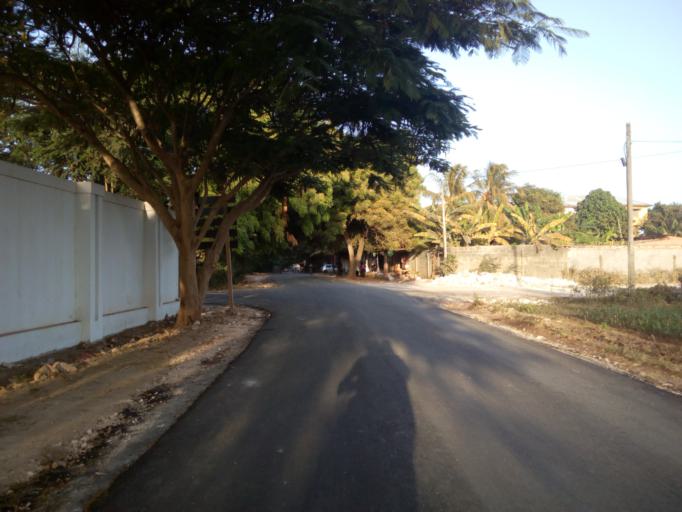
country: TZ
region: Zanzibar Urban/West
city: Zanzibar
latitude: -6.2087
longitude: 39.2044
